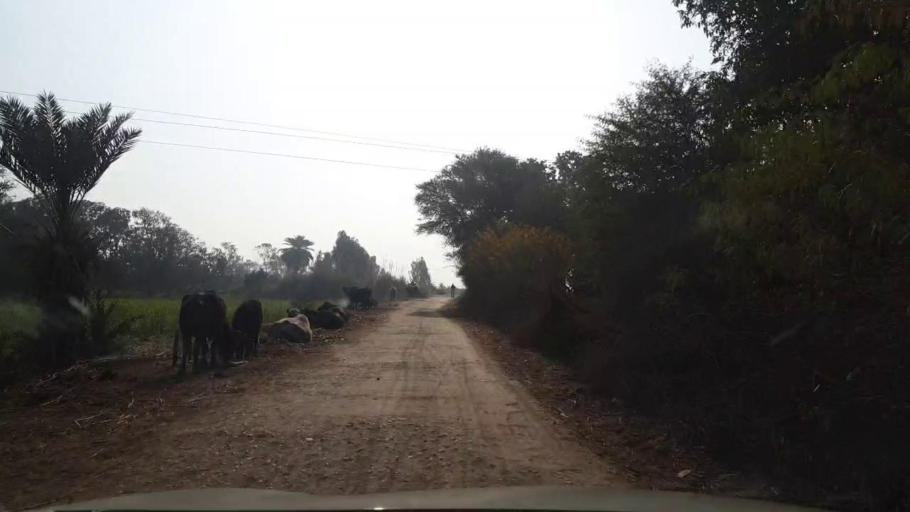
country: PK
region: Sindh
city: Matiari
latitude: 25.6867
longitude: 68.5227
